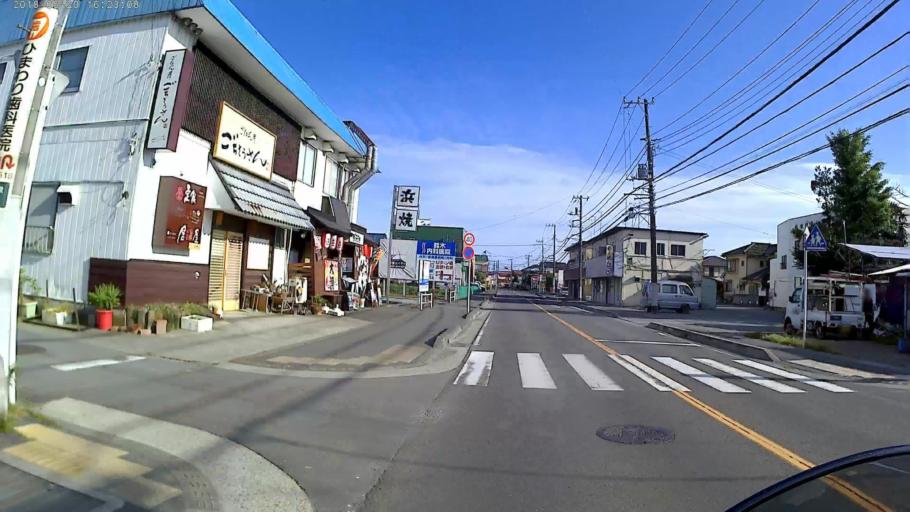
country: JP
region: Kanagawa
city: Odawara
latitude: 35.2930
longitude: 139.1484
